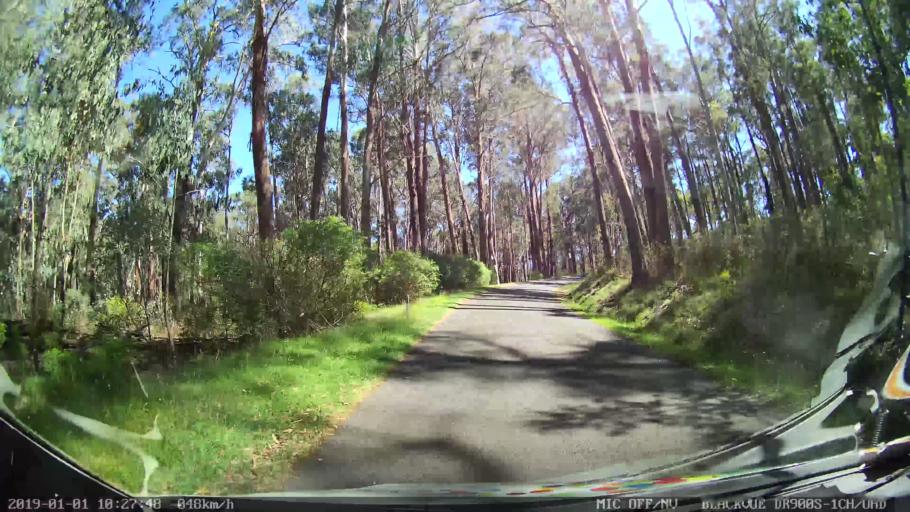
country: AU
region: New South Wales
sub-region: Snowy River
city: Jindabyne
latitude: -36.0638
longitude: 148.2365
